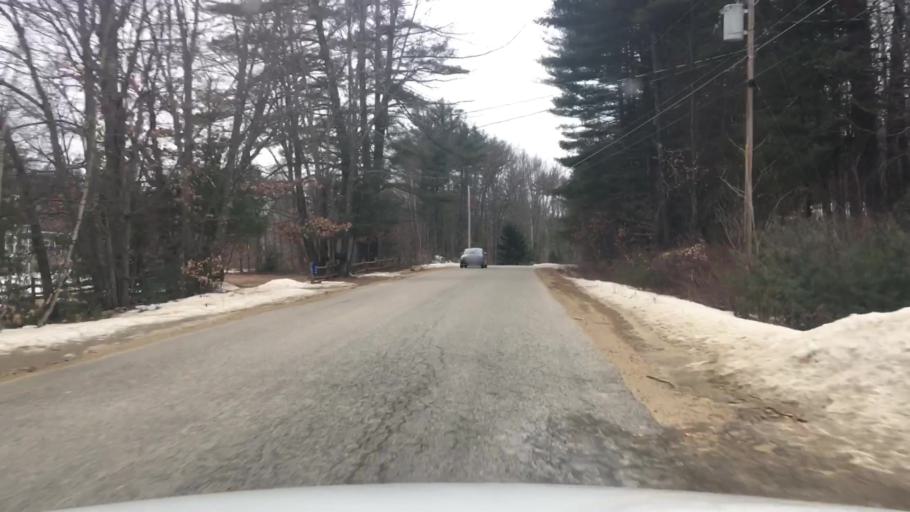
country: US
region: New Hampshire
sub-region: Strafford County
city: Rochester
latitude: 43.3632
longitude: -70.9704
